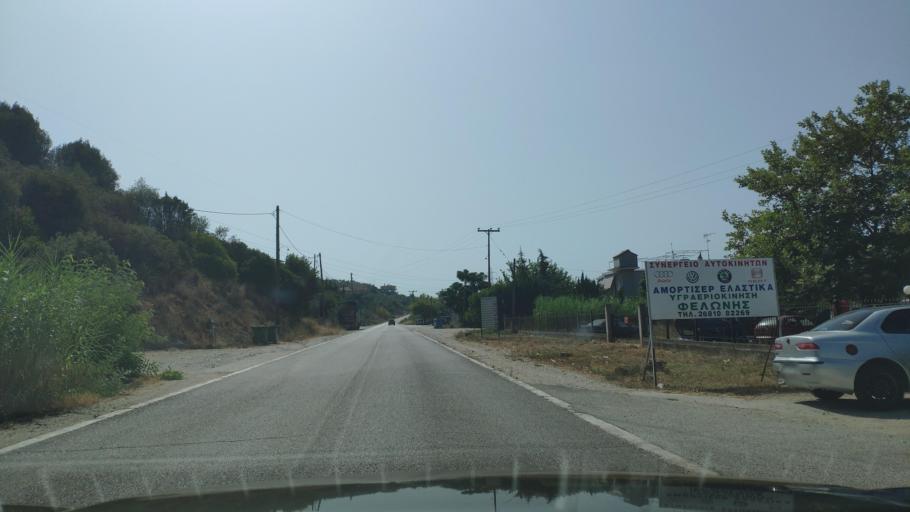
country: GR
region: Epirus
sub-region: Nomos Artas
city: Peta
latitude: 39.1615
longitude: 21.0205
